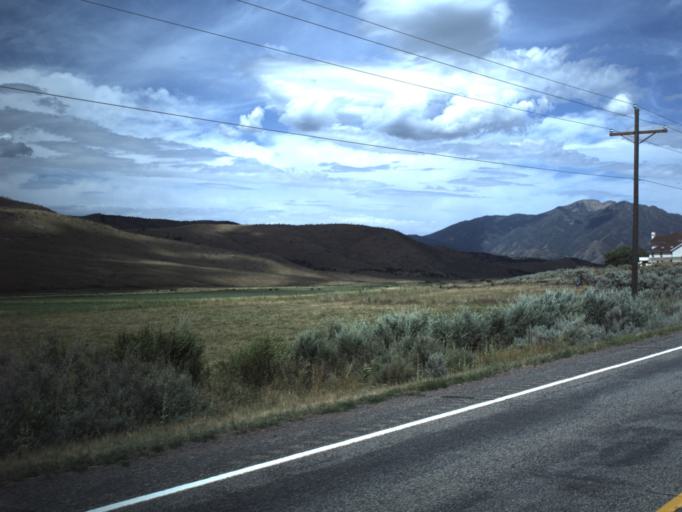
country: US
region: Utah
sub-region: Sanpete County
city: Fairview
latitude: 39.8291
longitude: -111.5112
